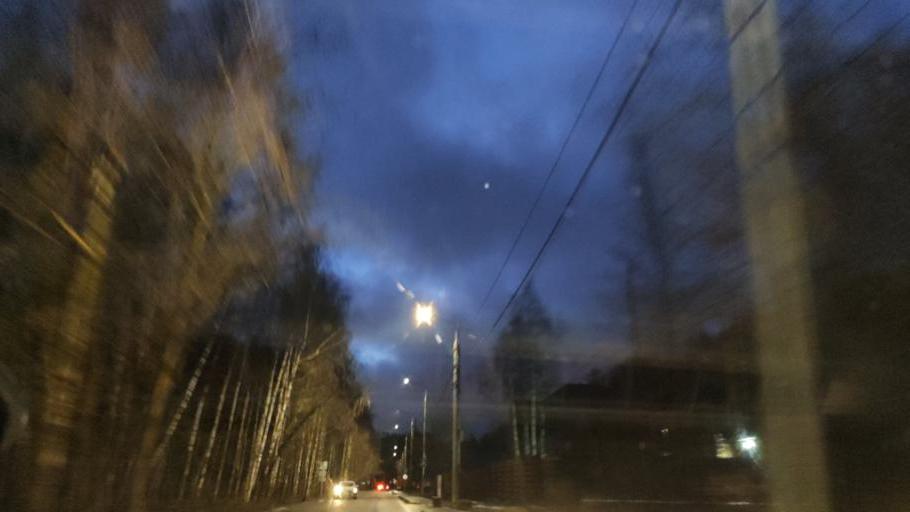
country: RU
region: Moscow
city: Annino
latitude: 55.5463
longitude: 37.6167
